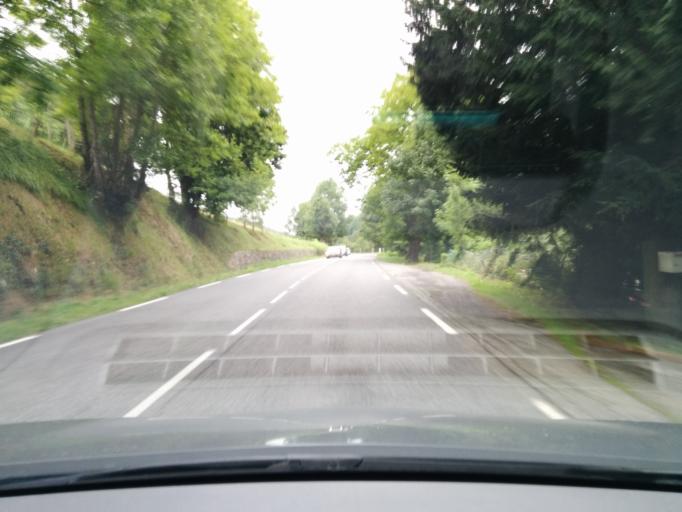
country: FR
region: Midi-Pyrenees
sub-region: Departement des Hautes-Pyrenees
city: La Barthe-de-Neste
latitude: 42.9843
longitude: 0.3758
